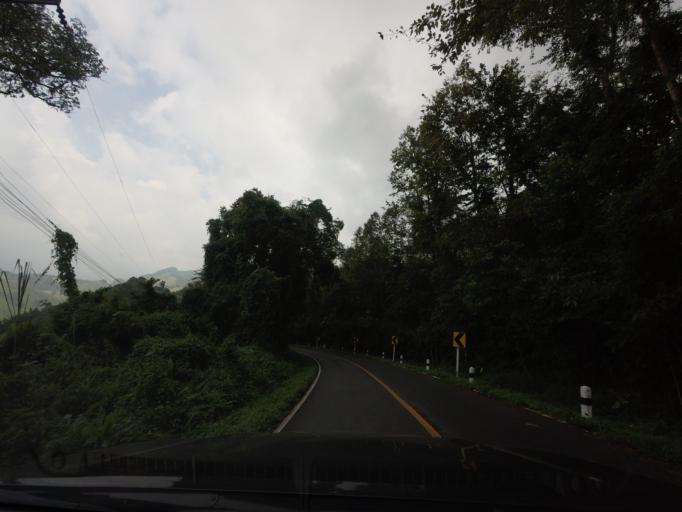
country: TH
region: Nan
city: Bo Kluea
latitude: 19.1956
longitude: 101.0519
